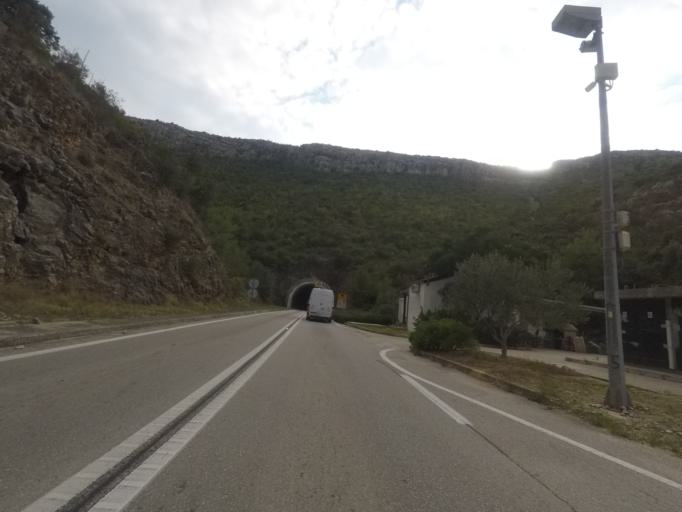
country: HR
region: Splitsko-Dalmatinska
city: Stari Grad
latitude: 43.1659
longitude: 16.5569
